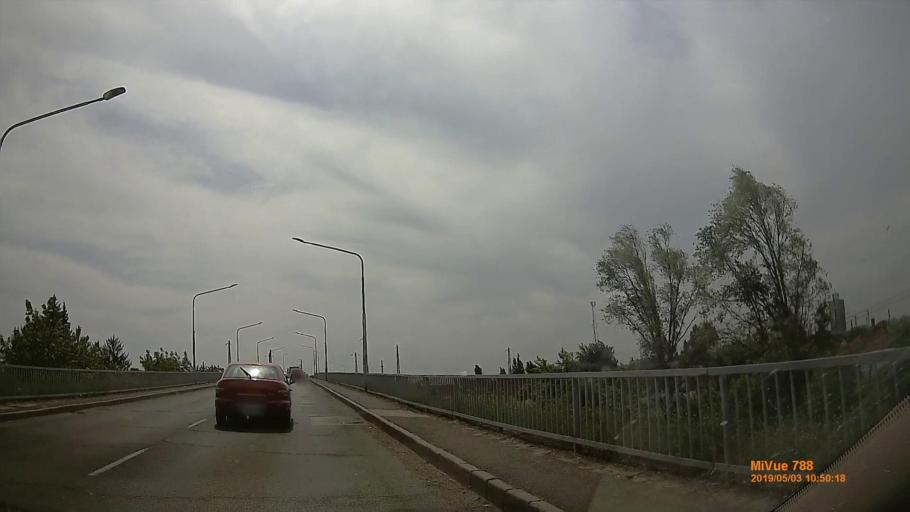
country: HU
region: Jasz-Nagykun-Szolnok
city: Szolnok
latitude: 47.1870
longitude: 20.1804
